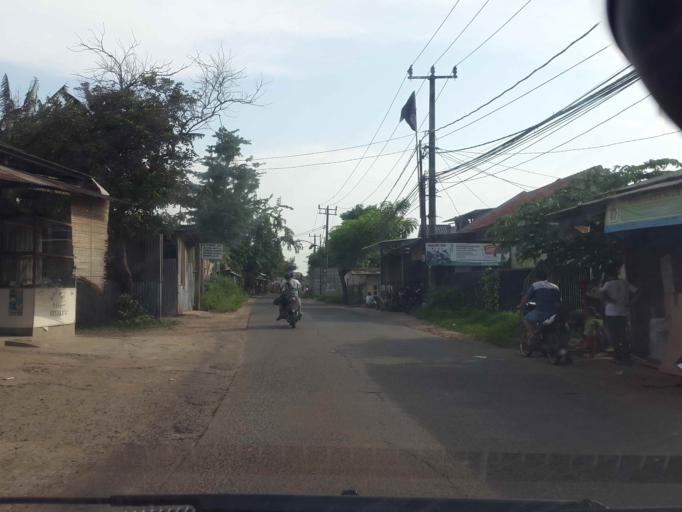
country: ID
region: West Java
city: Ciputat
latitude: -6.2721
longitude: 106.6705
